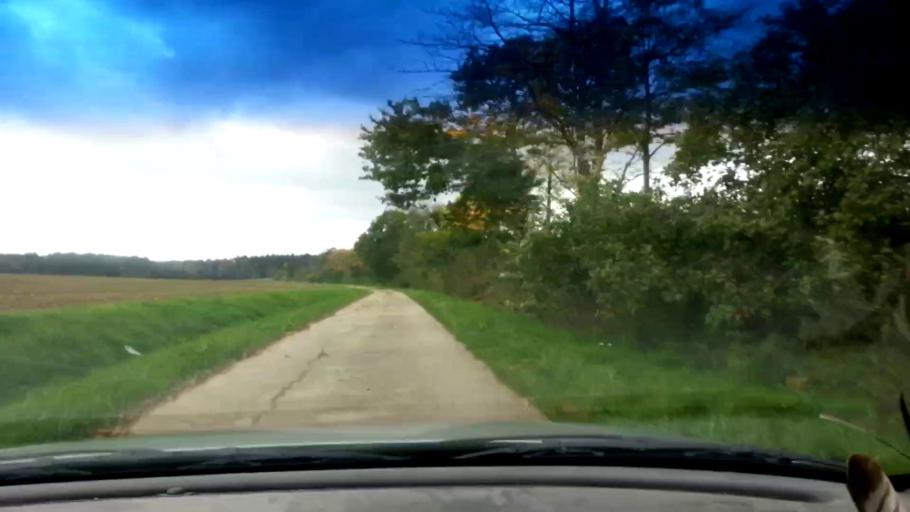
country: DE
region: Bavaria
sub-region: Upper Franconia
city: Schesslitz
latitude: 49.9957
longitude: 10.9892
